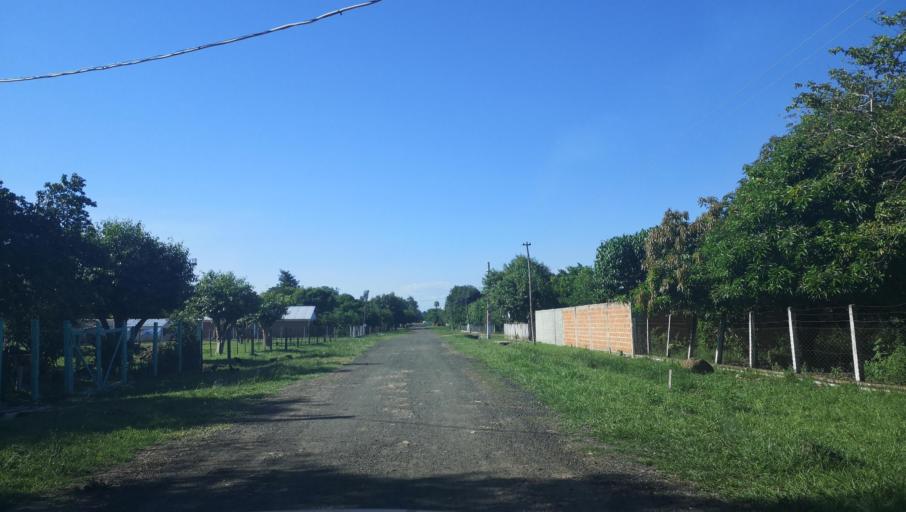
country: PY
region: Caaguazu
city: Carayao
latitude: -25.1997
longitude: -56.4019
